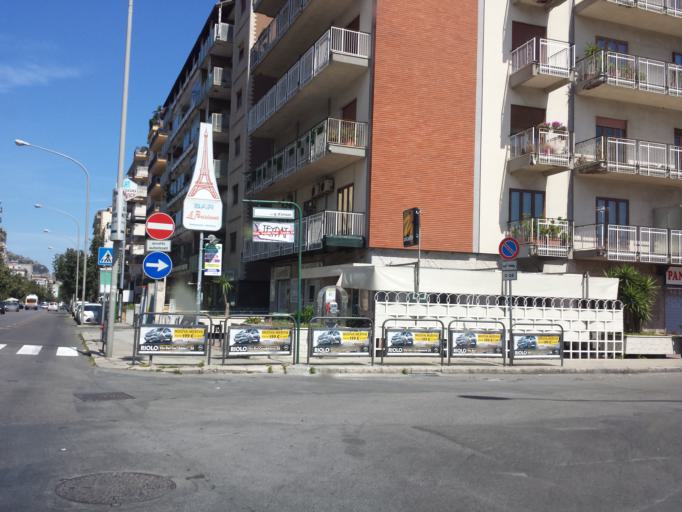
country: IT
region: Sicily
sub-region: Palermo
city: Palermo
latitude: 38.1402
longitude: 13.3322
